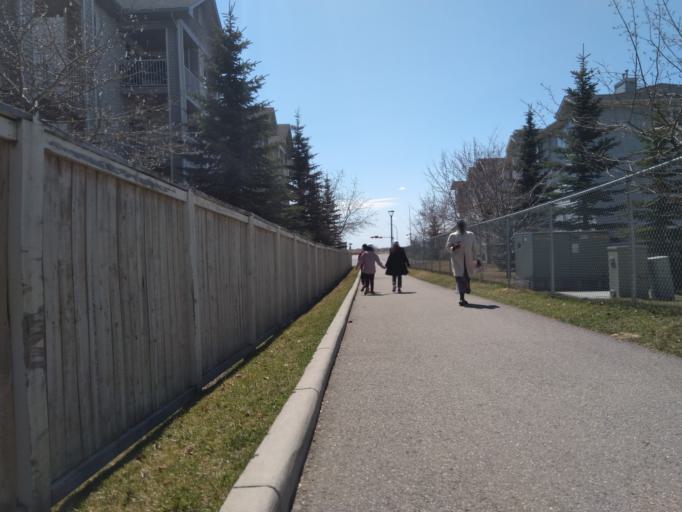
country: CA
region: Alberta
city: Chestermere
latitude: 51.0395
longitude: -113.9302
